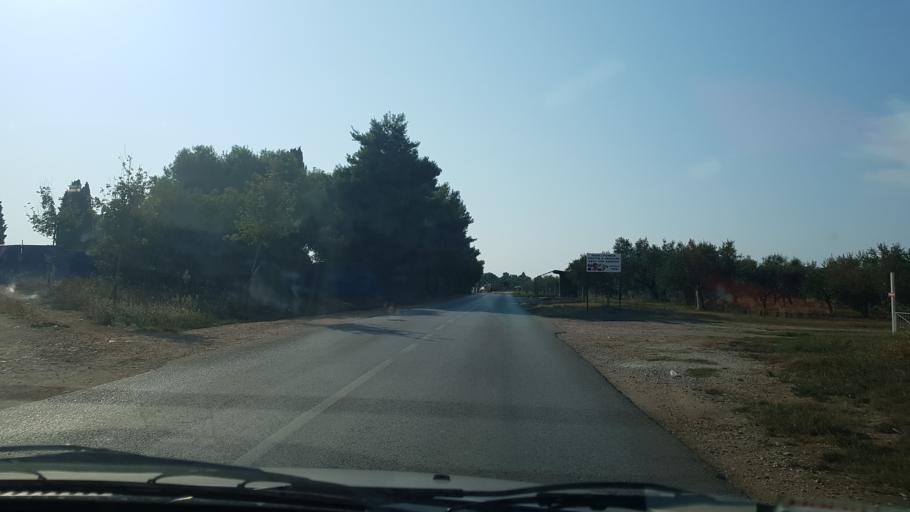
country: HR
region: Istarska
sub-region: Grad Rovinj
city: Rovinj
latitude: 45.1061
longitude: 13.6280
